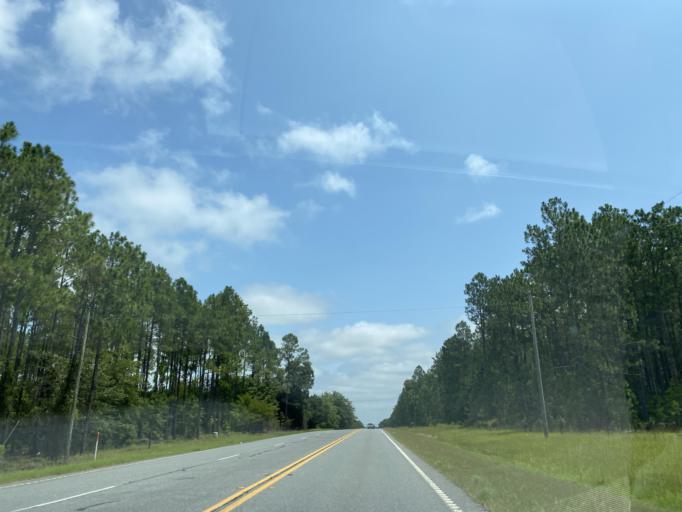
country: US
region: Georgia
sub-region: Wheeler County
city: Alamo
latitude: 32.1166
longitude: -82.8049
